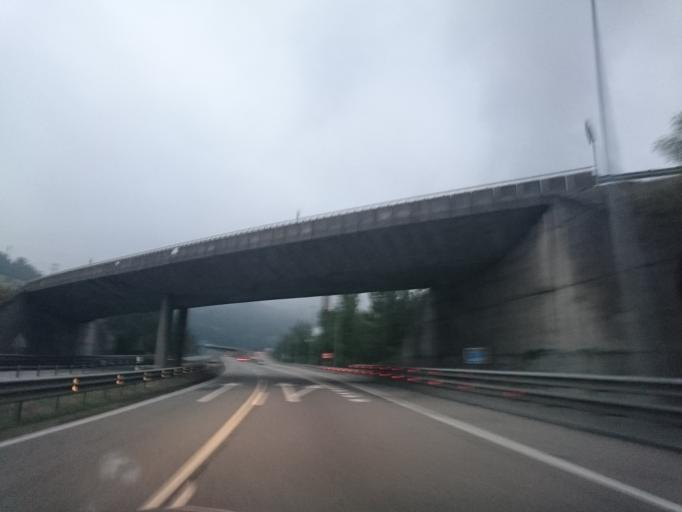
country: ES
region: Asturias
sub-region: Province of Asturias
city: Mieres
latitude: 43.2765
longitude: -5.8095
